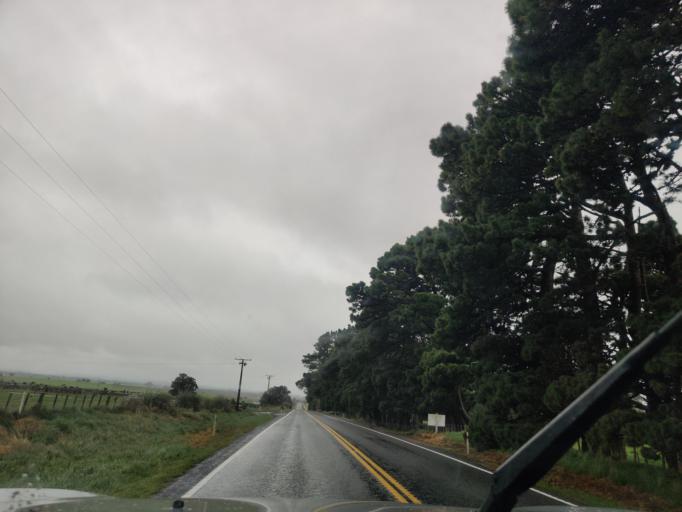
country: NZ
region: Manawatu-Wanganui
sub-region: Palmerston North City
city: Palmerston North
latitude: -40.0388
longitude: 176.2542
